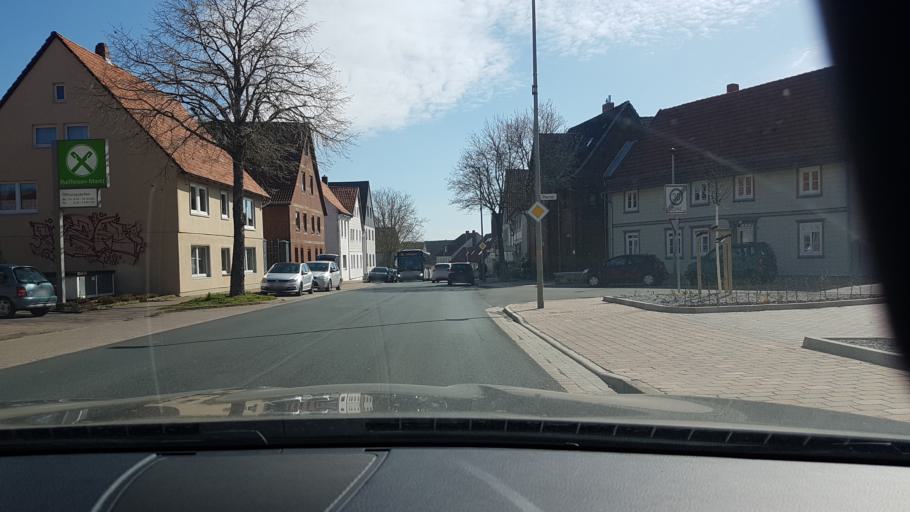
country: DE
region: Lower Saxony
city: Elze
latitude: 52.1845
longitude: 9.6726
